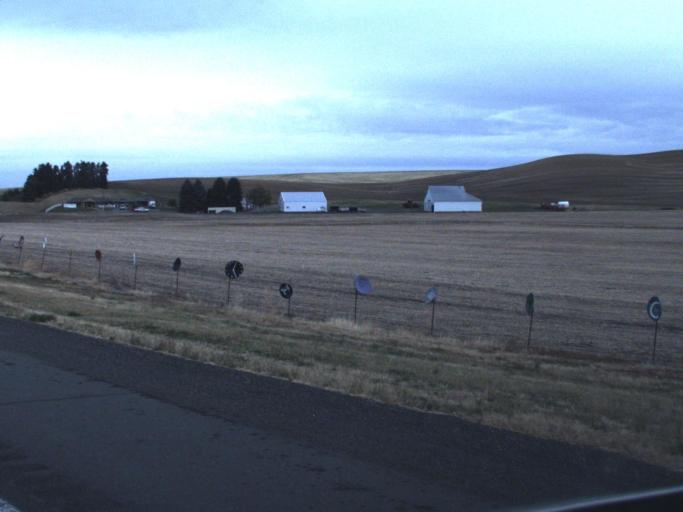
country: US
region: Washington
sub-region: Asotin County
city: Clarkston
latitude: 46.4898
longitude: -117.0724
